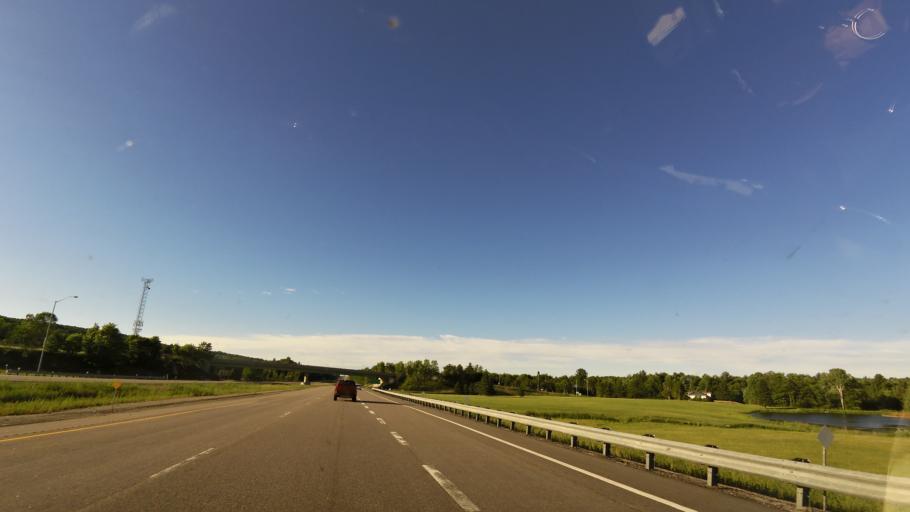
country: CA
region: Ontario
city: Barrie
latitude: 44.6235
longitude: -79.6603
